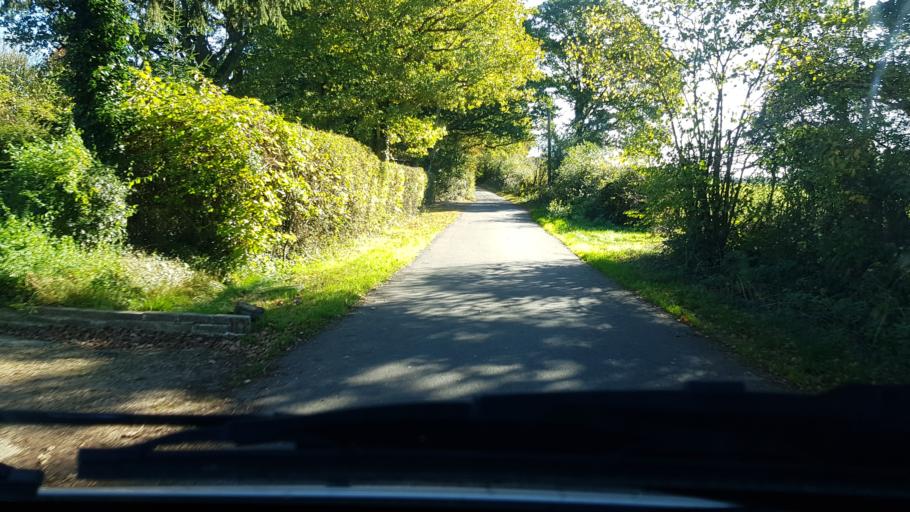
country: GB
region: England
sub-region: Surrey
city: Ockley
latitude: 51.1250
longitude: -0.3599
